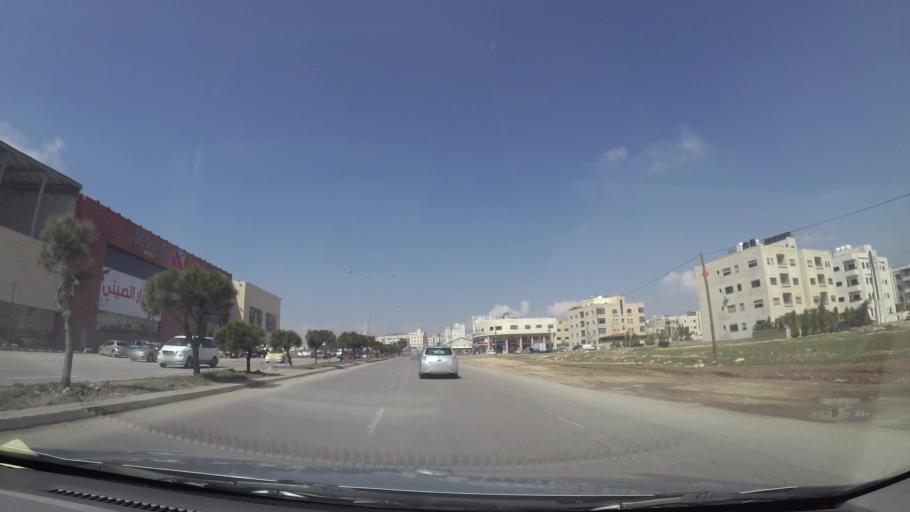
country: JO
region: Amman
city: Al Bunayyat ash Shamaliyah
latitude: 31.9039
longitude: 35.8883
